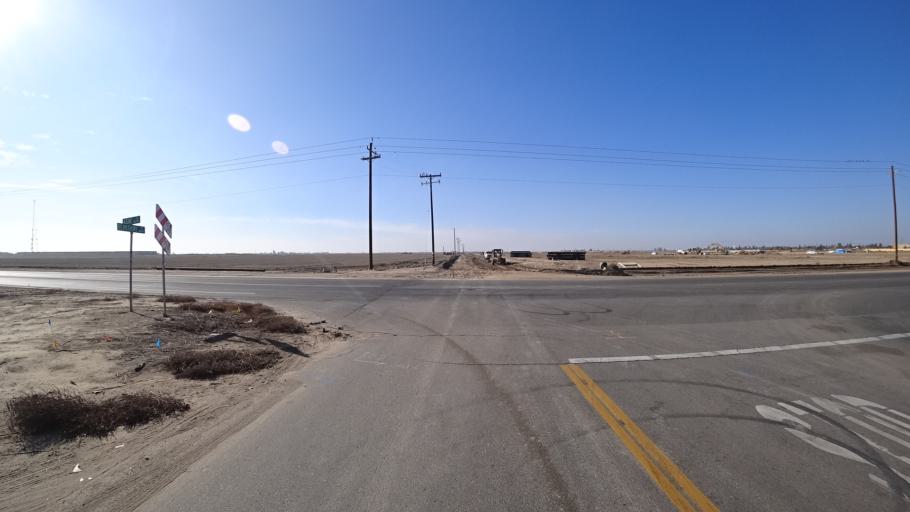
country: US
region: California
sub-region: Kern County
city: Greenfield
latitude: 35.2888
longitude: -119.0742
